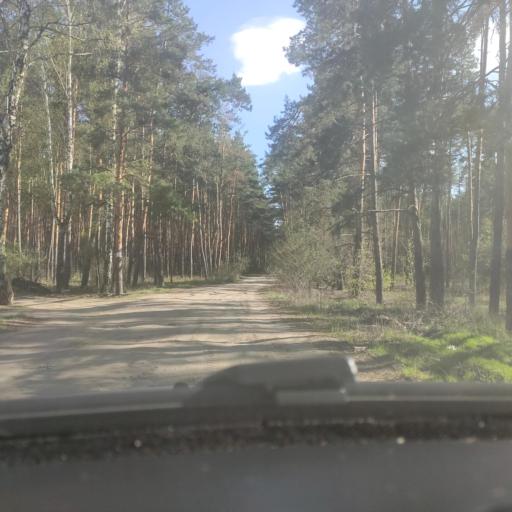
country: RU
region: Voronezj
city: Somovo
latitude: 51.7502
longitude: 39.3233
